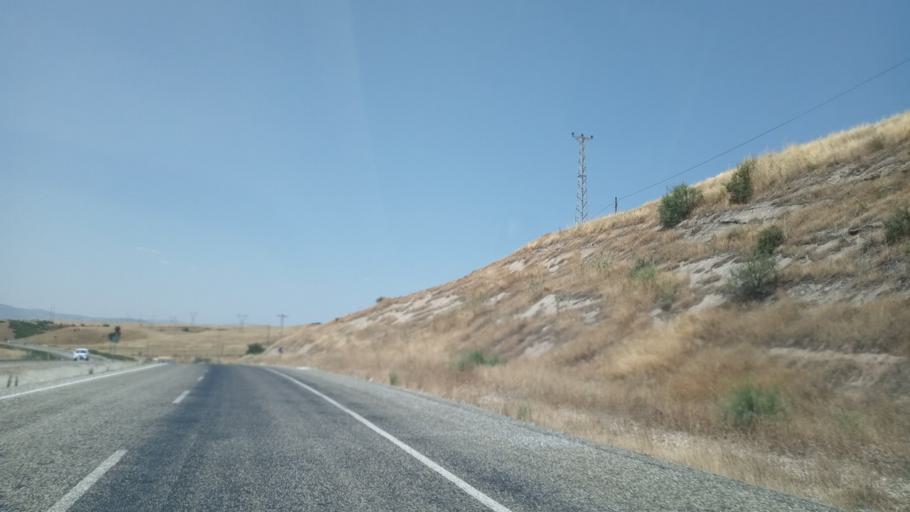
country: TR
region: Batman
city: Bekirhan
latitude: 38.1581
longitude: 41.3433
